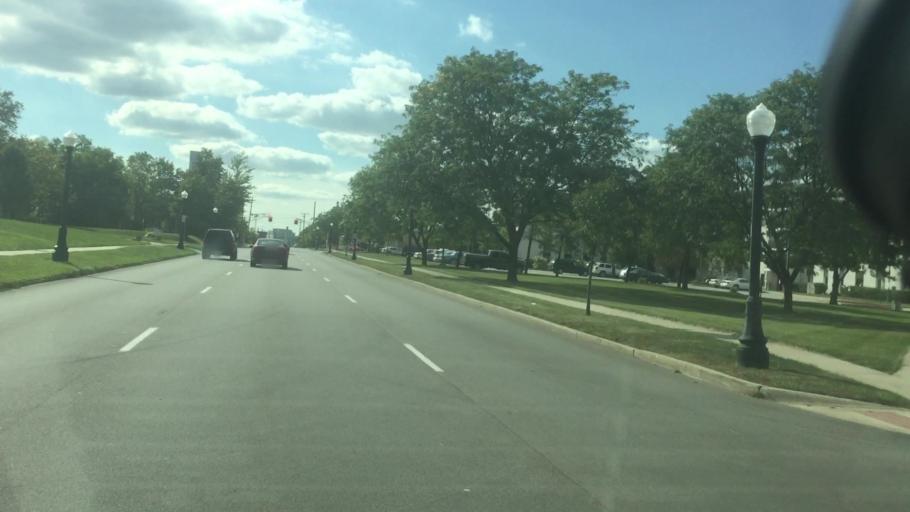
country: US
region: Indiana
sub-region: Allen County
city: Fort Wayne
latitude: 41.0789
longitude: -85.1236
